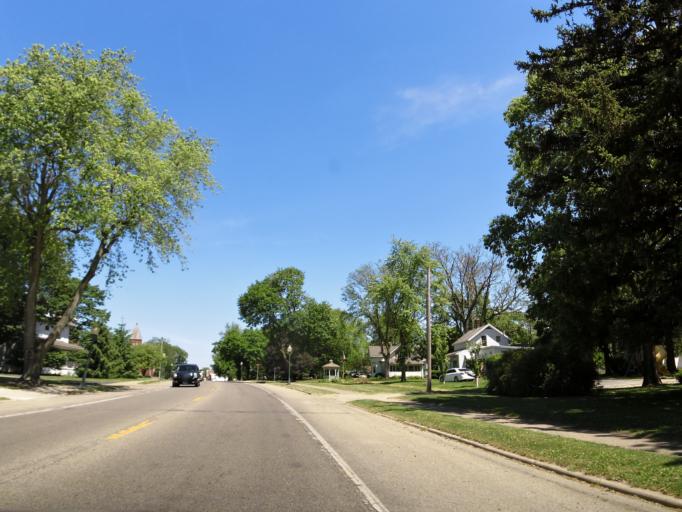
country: US
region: Illinois
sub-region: Vermilion County
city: Rossville
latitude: 40.3760
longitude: -87.6675
